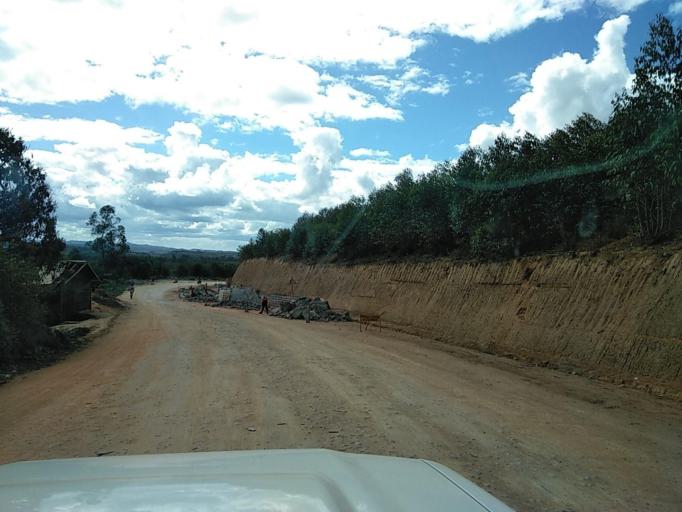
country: MG
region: Analamanga
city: Anjozorobe
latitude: -18.4412
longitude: 48.2646
